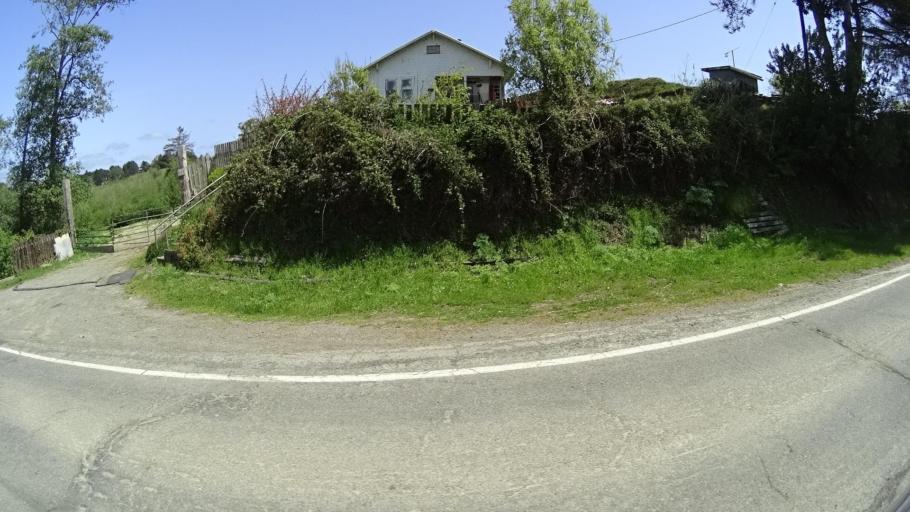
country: US
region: California
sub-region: Humboldt County
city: Ferndale
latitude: 40.6366
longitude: -124.2239
